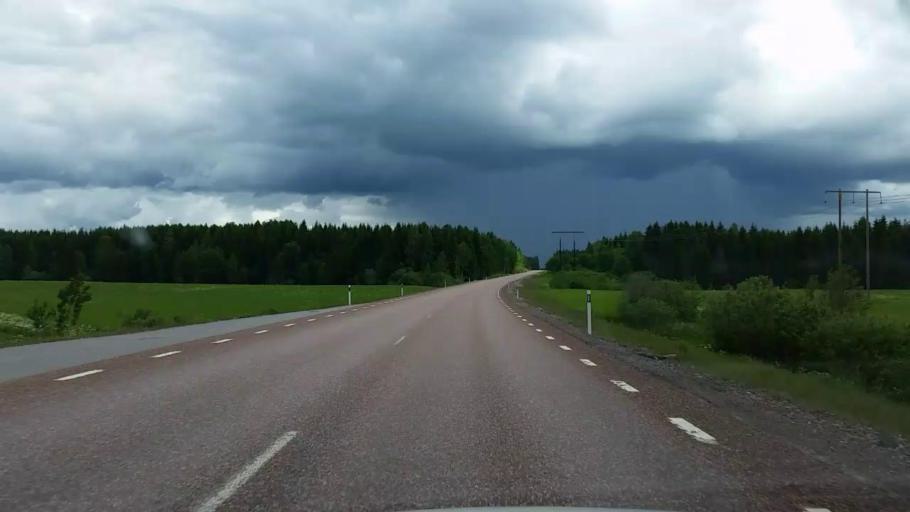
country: SE
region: Gaevleborg
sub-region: Hofors Kommun
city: Hofors
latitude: 60.5394
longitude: 16.4620
